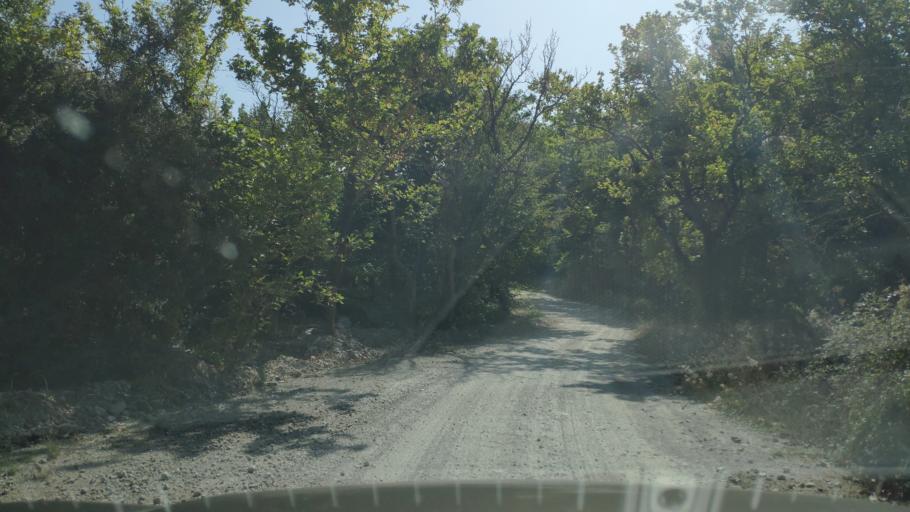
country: GR
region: West Greece
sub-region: Nomos Achaias
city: Aiyira
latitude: 37.9428
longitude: 22.3178
